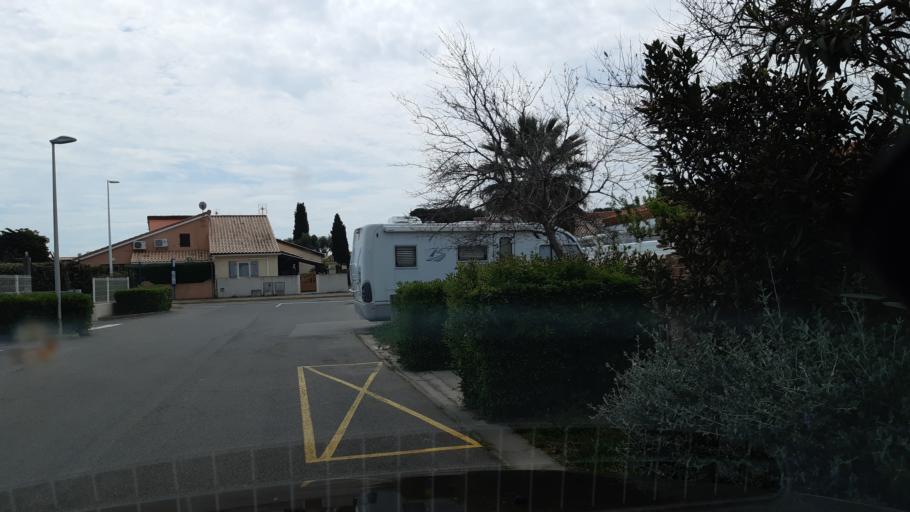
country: FR
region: Languedoc-Roussillon
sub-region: Departement de l'Aude
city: Gruissan
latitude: 43.1147
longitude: 3.1027
